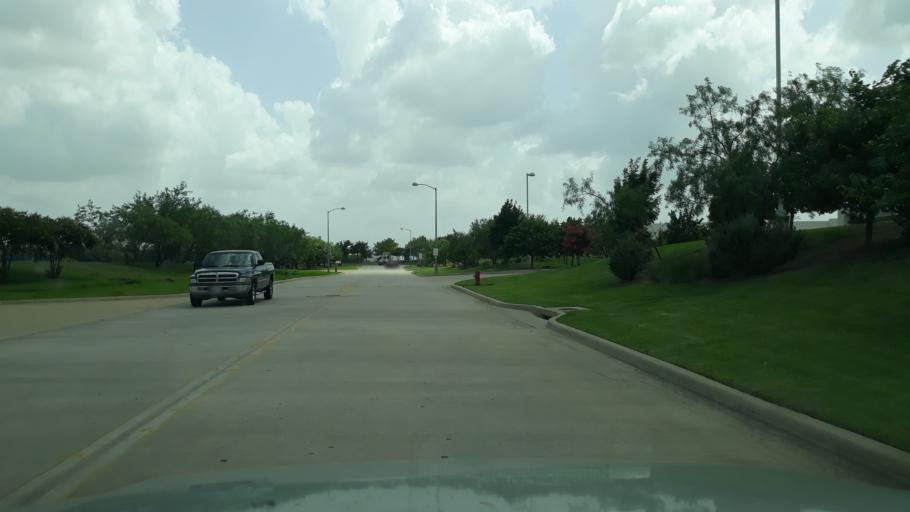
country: US
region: Texas
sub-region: Dallas County
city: Coppell
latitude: 32.9370
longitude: -97.0326
